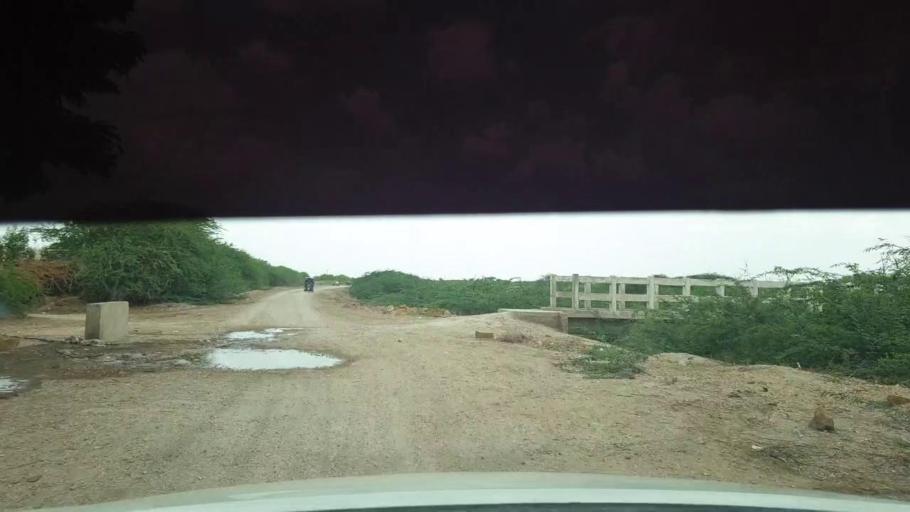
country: PK
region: Sindh
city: Kadhan
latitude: 24.4677
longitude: 69.0499
